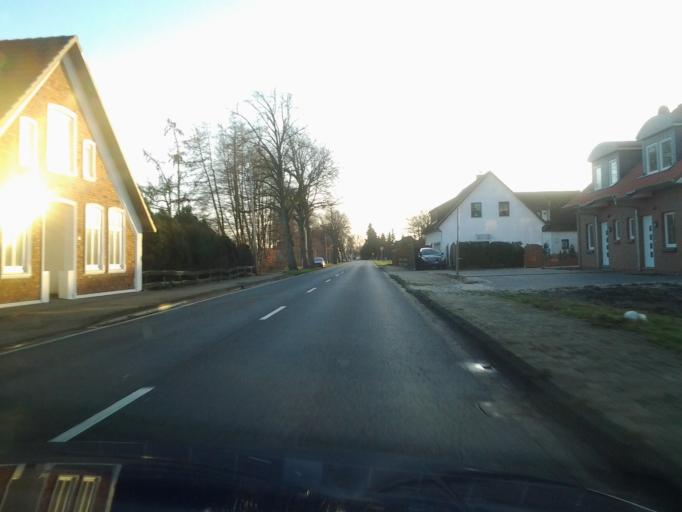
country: DE
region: Lower Saxony
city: Lilienthal
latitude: 53.1678
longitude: 8.9277
